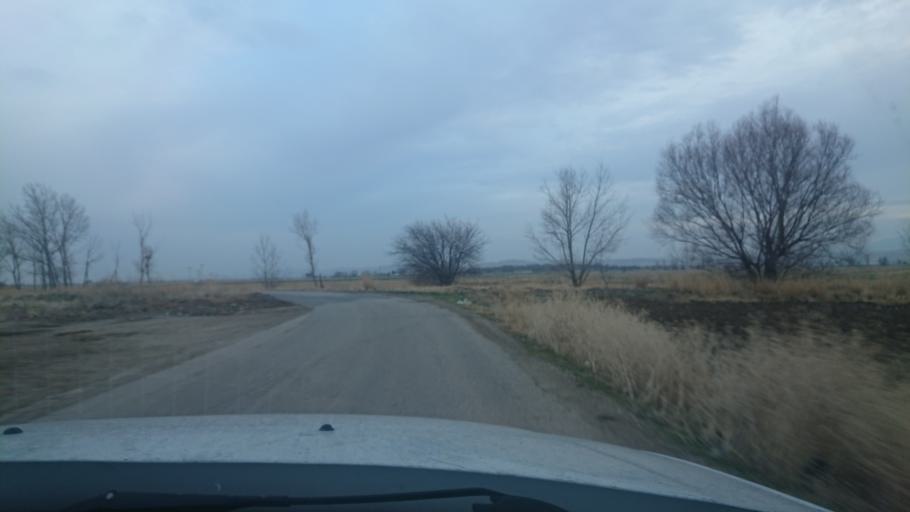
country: TR
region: Aksaray
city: Yesilova
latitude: 38.4462
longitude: 33.8365
